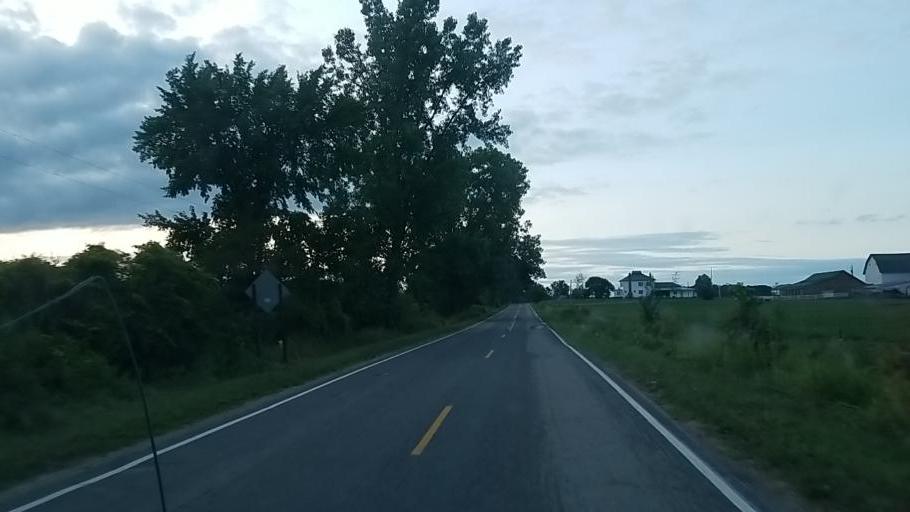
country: US
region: Michigan
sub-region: Muskegon County
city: Twin Lake
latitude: 43.4701
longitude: -86.0793
